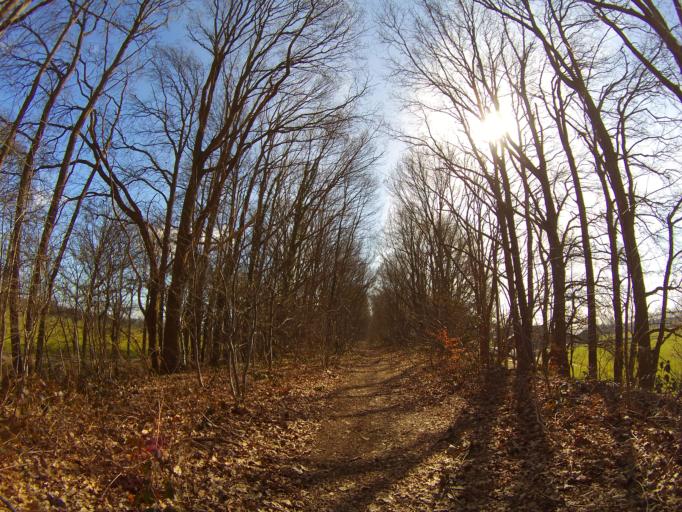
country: NL
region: Utrecht
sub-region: Gemeente Utrechtse Heuvelrug
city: Overberg
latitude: 52.0606
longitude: 5.4682
